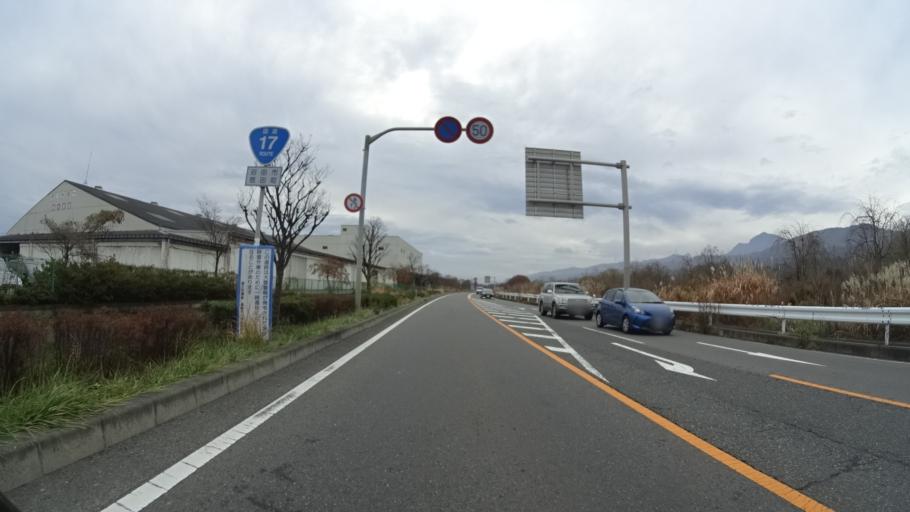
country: JP
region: Gunma
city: Numata
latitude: 36.6554
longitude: 139.0211
